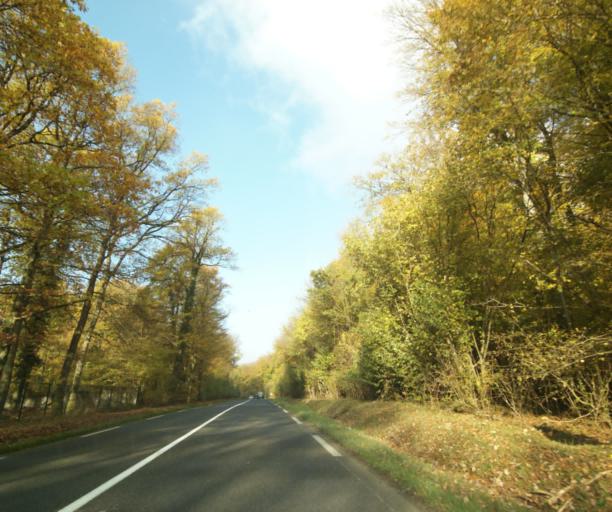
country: FR
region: Lorraine
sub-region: Departement de Meurthe-et-Moselle
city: Briey
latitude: 49.2617
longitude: 5.9319
